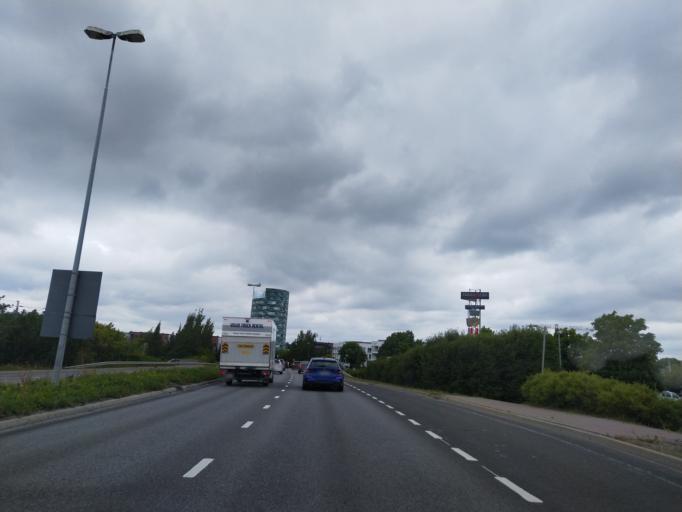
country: FI
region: Varsinais-Suomi
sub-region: Turku
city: Turku
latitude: 60.4584
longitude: 22.2895
